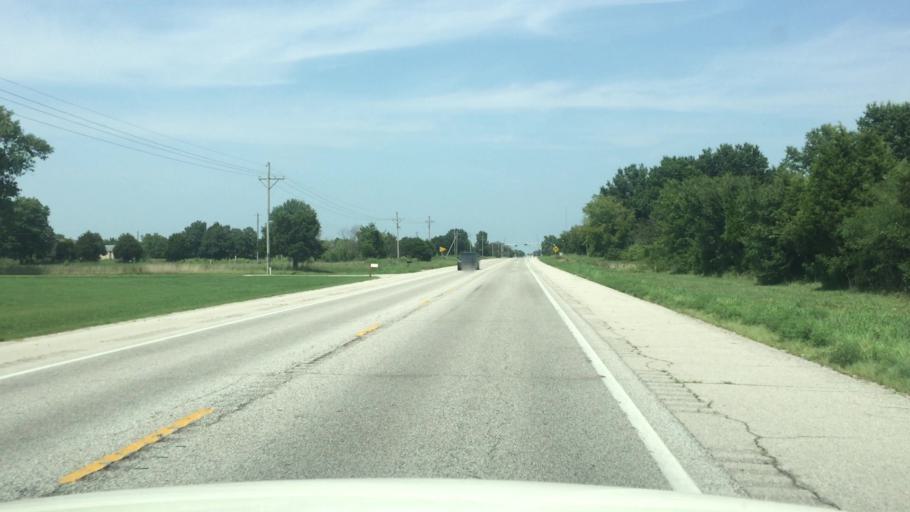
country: US
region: Kansas
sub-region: Cherokee County
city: Galena
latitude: 37.1098
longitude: -94.7043
